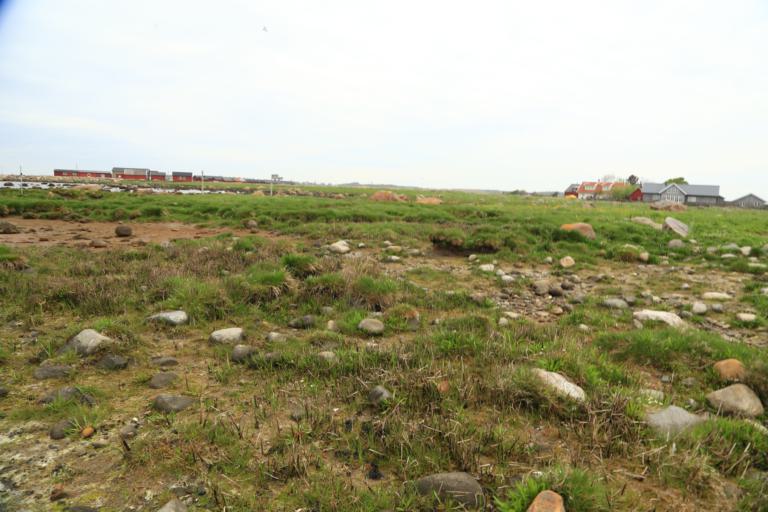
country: SE
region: Halland
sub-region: Varbergs Kommun
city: Traslovslage
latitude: 57.0261
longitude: 12.3134
